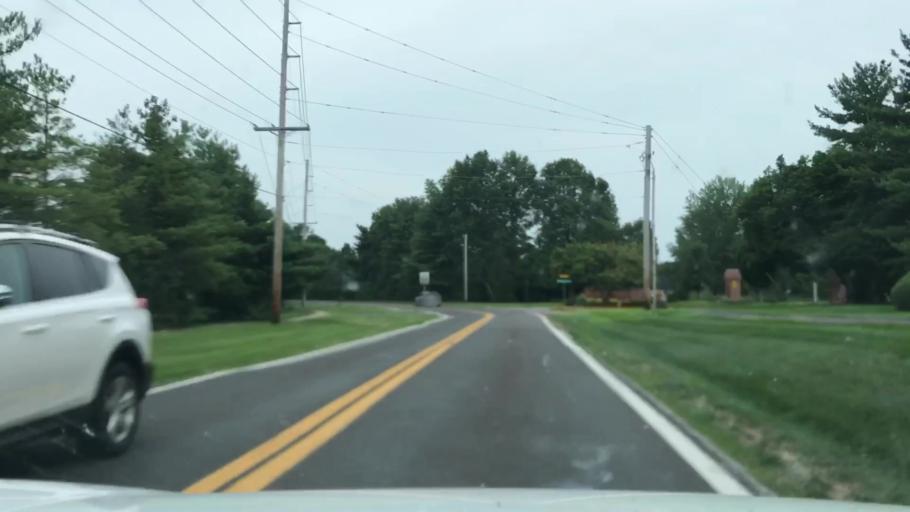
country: US
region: Missouri
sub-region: Saint Louis County
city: Clarkson Valley
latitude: 38.6287
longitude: -90.5973
